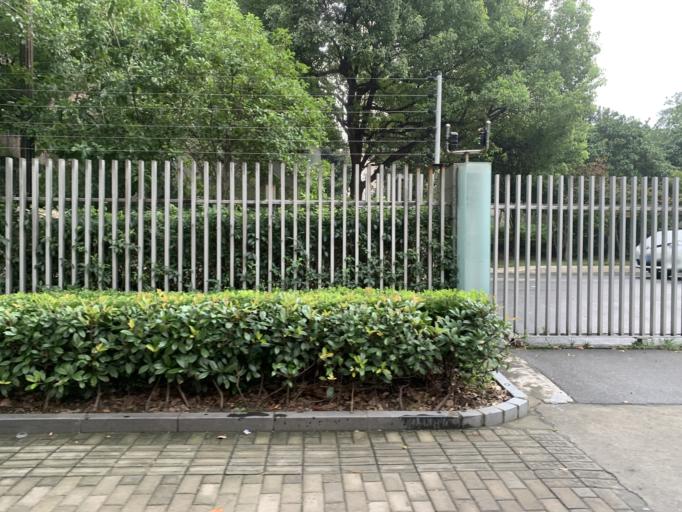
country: CN
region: Shanghai Shi
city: Huamu
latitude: 31.2283
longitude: 121.5620
